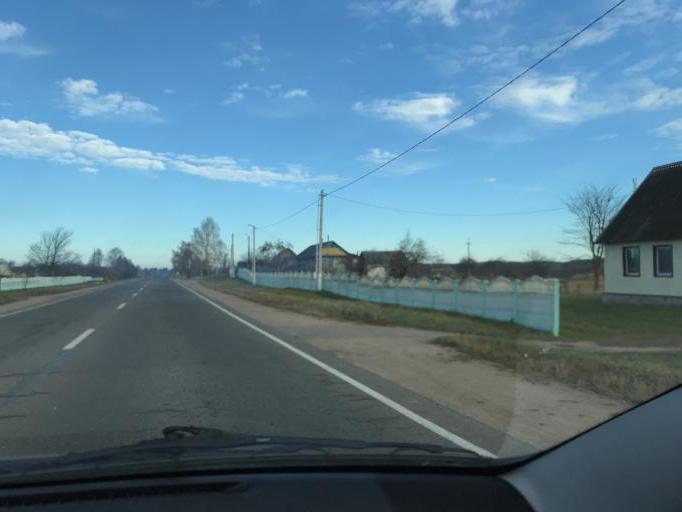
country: BY
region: Vitebsk
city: Haradok
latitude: 55.4848
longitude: 29.9679
